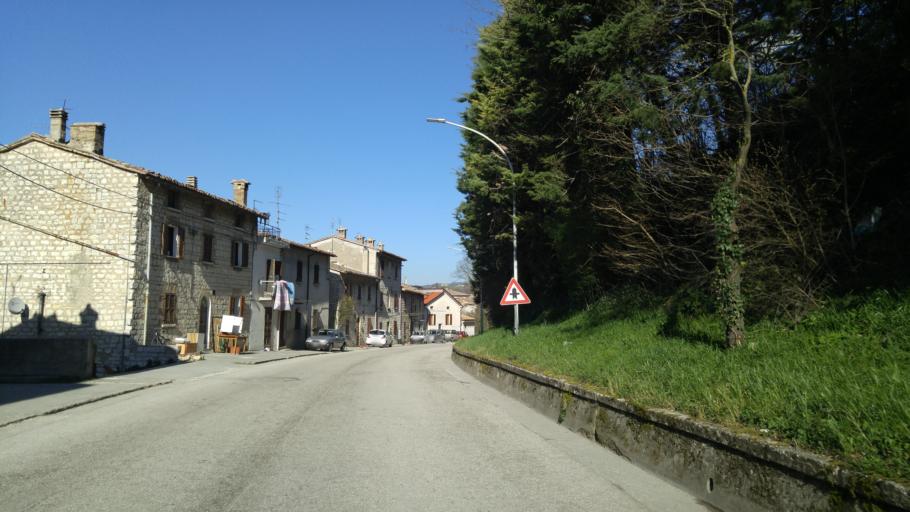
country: IT
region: The Marches
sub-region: Provincia di Pesaro e Urbino
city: Cagli
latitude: 43.5455
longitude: 12.6443
